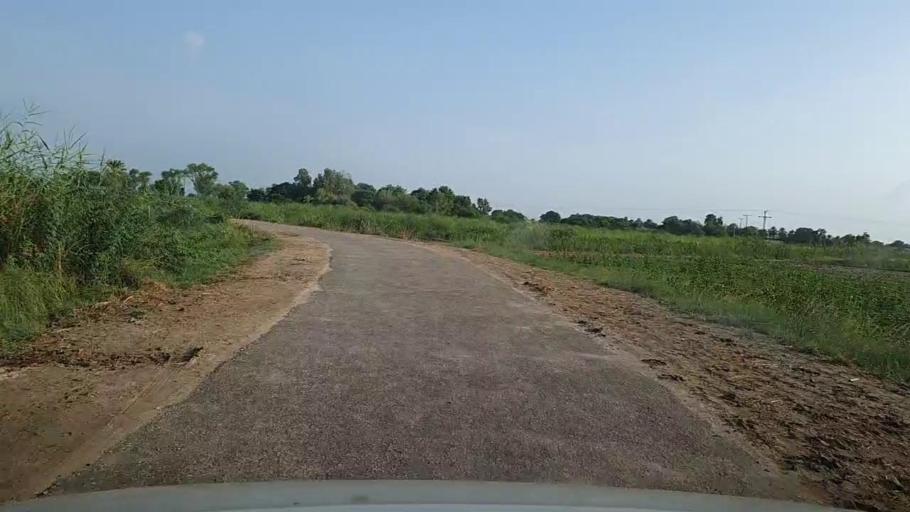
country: PK
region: Sindh
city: Pad Idan
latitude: 26.8028
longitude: 68.2355
